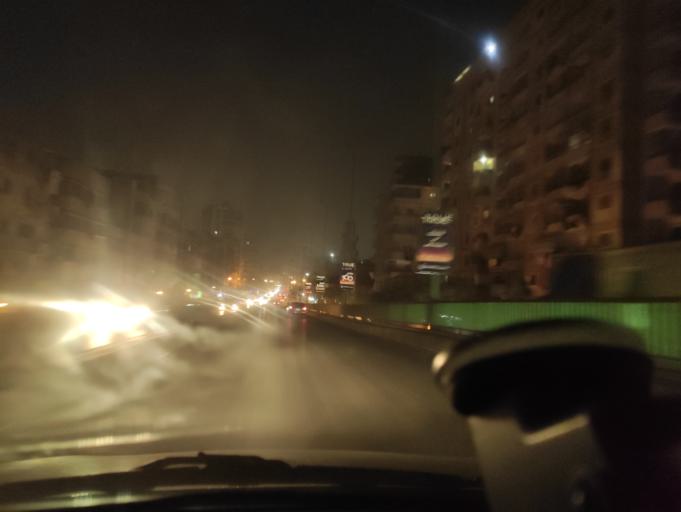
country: EG
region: Muhafazat al Qahirah
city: Cairo
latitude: 30.0924
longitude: 31.2777
